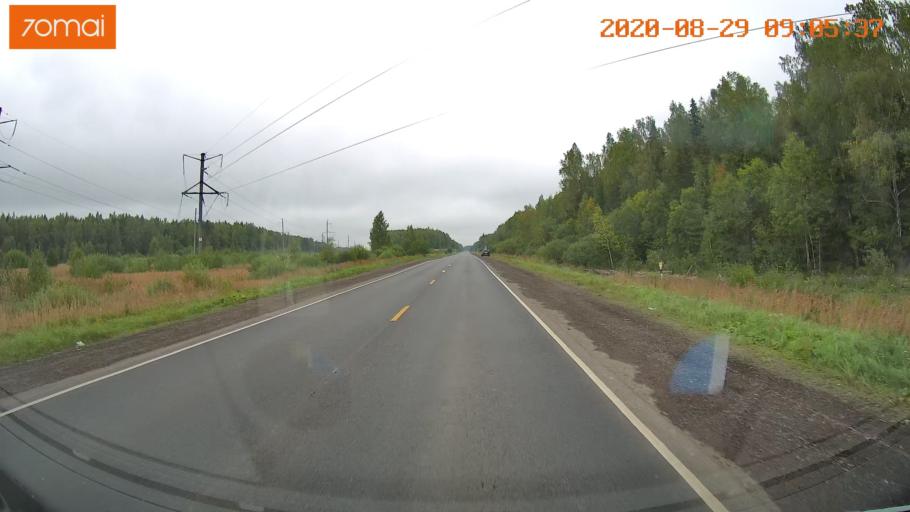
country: RU
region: Ivanovo
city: Navoloki
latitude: 57.3608
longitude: 42.0037
